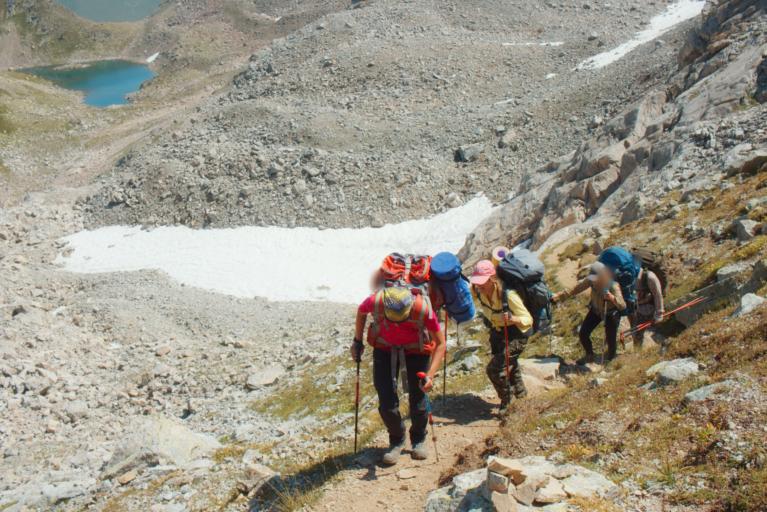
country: RU
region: Karachayevo-Cherkesiya
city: Nizhniy Arkhyz
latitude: 43.4574
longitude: 41.2186
